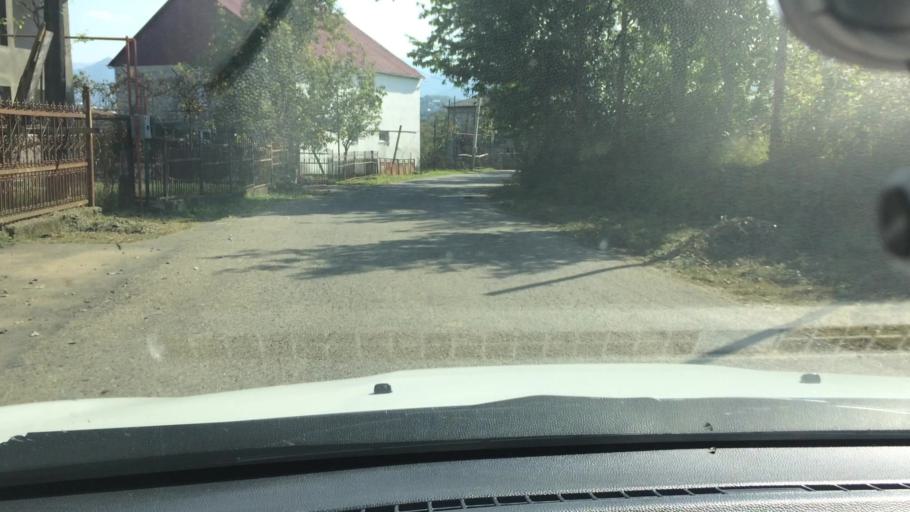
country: GE
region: Ajaria
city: Kobuleti
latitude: 41.8154
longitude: 41.8223
